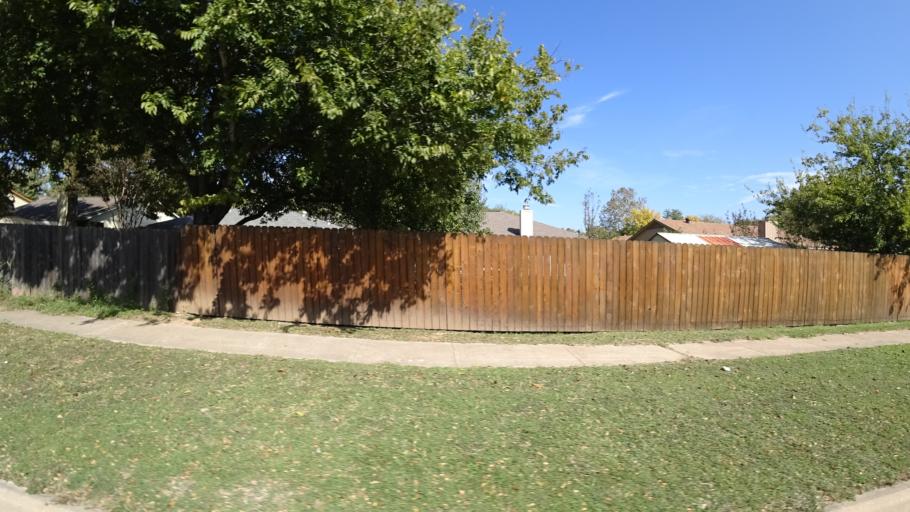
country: US
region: Texas
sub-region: Travis County
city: Shady Hollow
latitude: 30.2108
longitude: -97.8236
